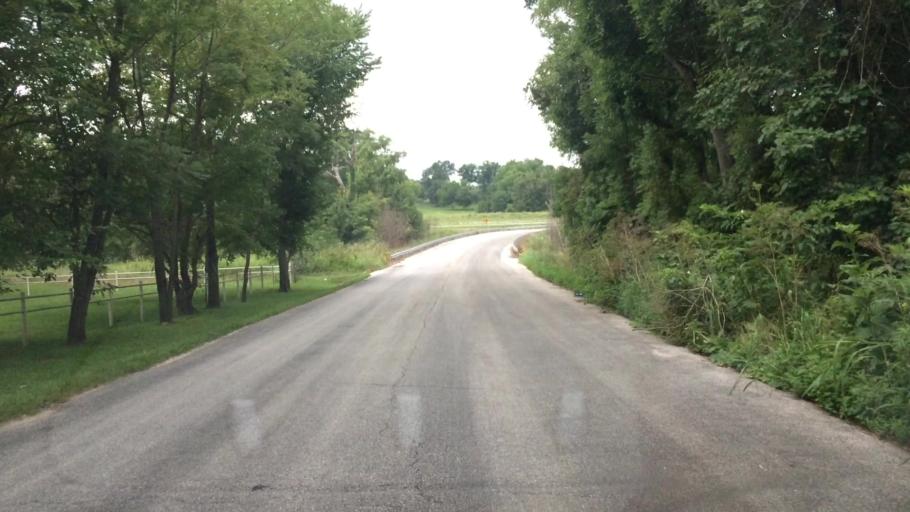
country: US
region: Missouri
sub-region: Webster County
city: Marshfield
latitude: 37.3052
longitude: -92.9846
